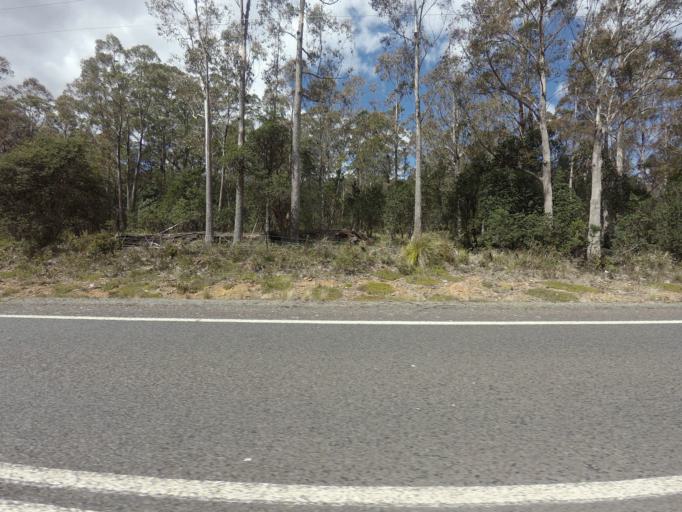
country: AU
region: Tasmania
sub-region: Northern Midlands
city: Evandale
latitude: -42.0061
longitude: 147.7235
